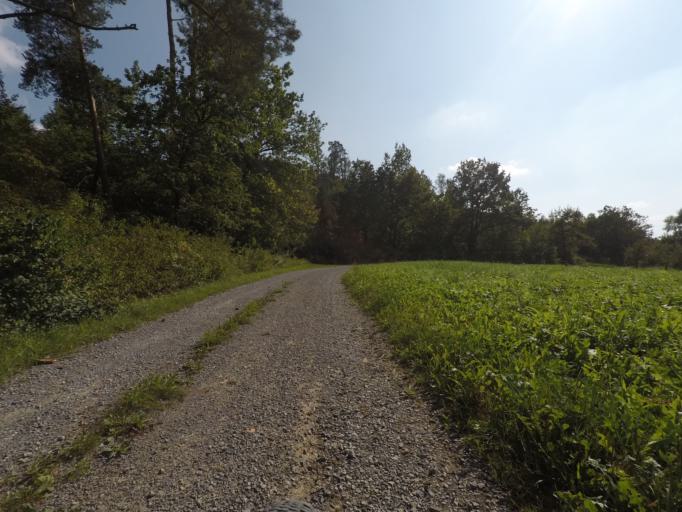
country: DE
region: Baden-Wuerttemberg
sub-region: Regierungsbezirk Stuttgart
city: Weil im Schonbuch
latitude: 48.6397
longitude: 9.0700
